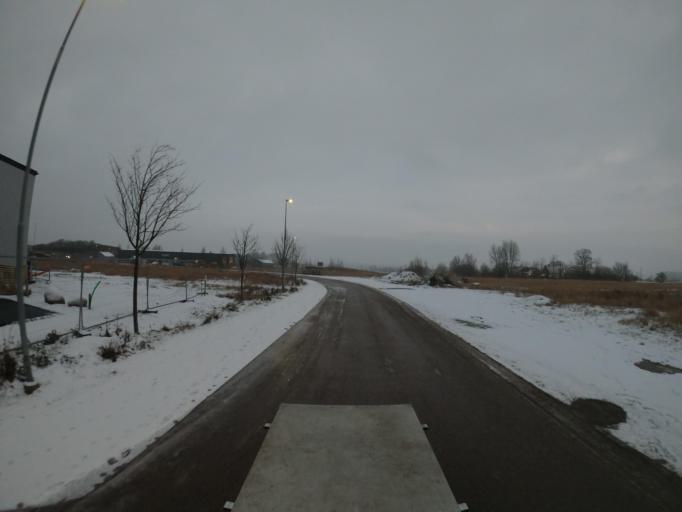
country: SE
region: Skane
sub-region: Svedala Kommun
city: Svedala
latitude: 55.5119
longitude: 13.2633
